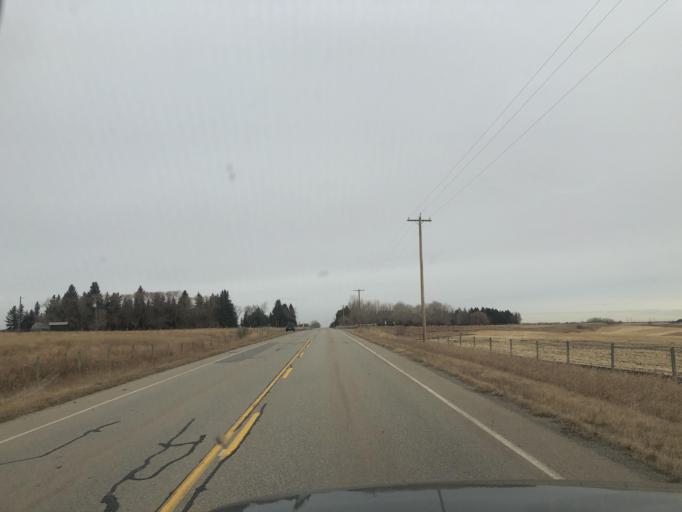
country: CA
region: Alberta
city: Chestermere
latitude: 50.9874
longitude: -113.8654
